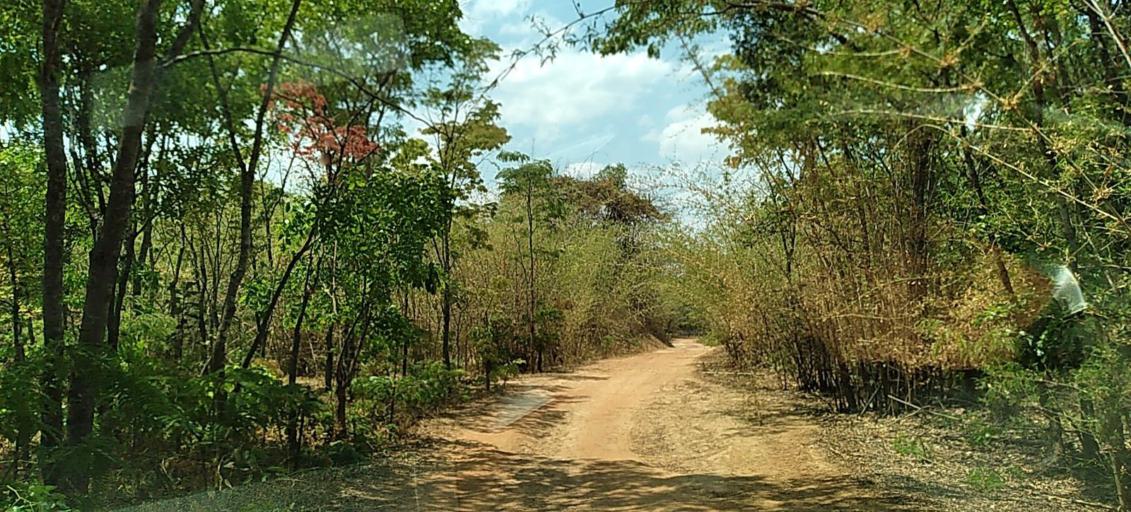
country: ZM
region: Copperbelt
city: Chililabombwe
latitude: -12.4877
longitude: 27.6393
